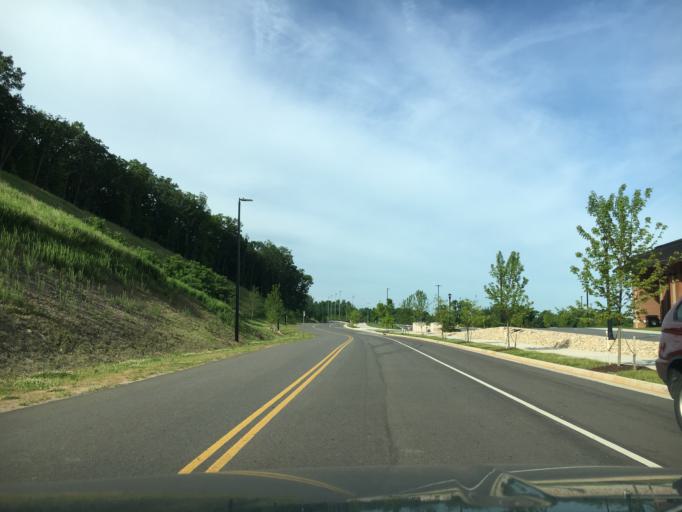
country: US
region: Virginia
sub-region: City of Lynchburg
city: West Lynchburg
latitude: 37.3614
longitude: -79.1610
